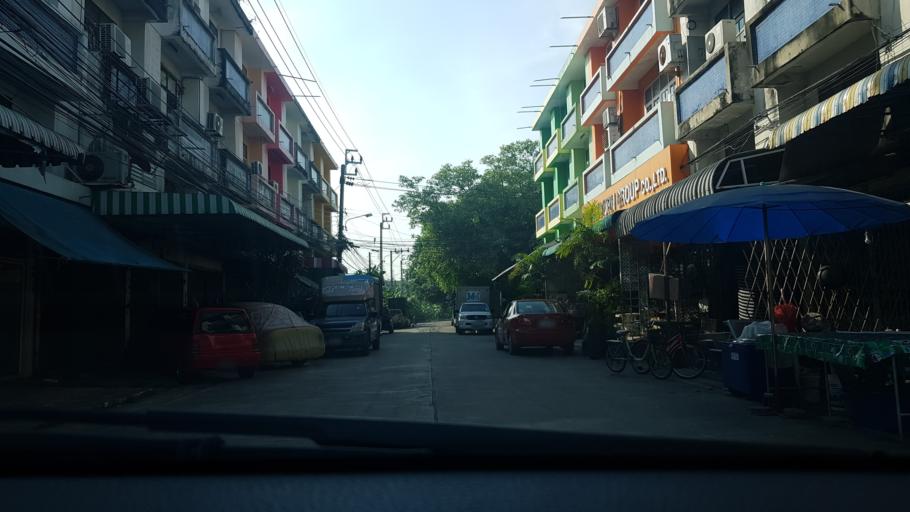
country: TH
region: Bangkok
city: Thawi Watthana
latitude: 13.7895
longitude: 100.3804
